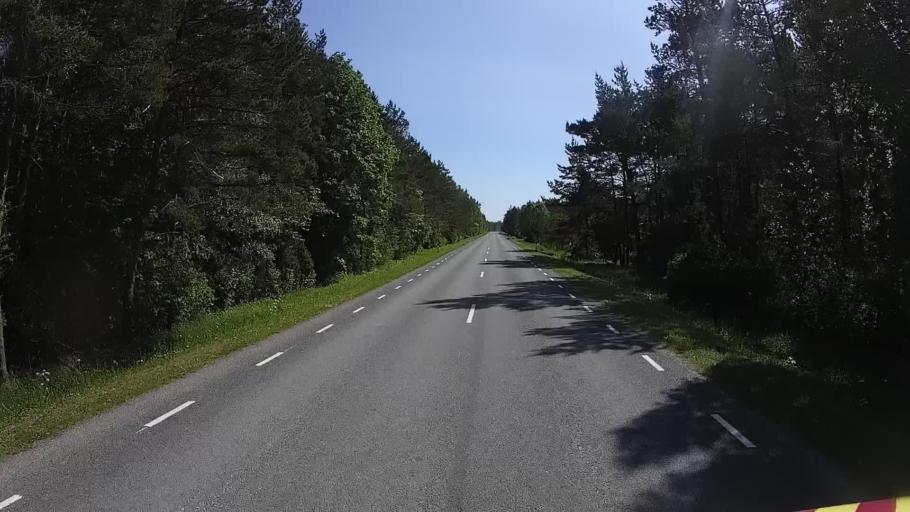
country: EE
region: Saare
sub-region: Kuressaare linn
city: Kuressaare
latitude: 58.3676
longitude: 22.4374
